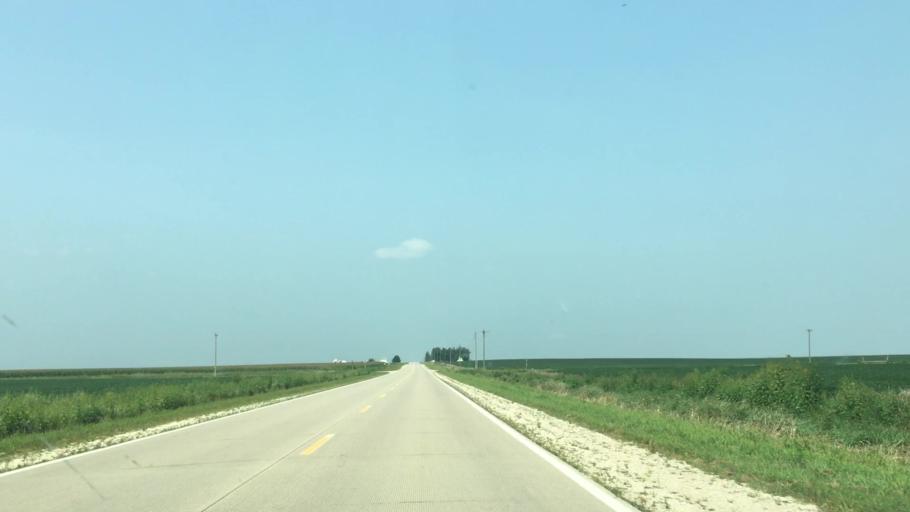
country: US
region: Iowa
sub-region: Fayette County
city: Oelwein
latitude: 42.7002
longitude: -91.8049
